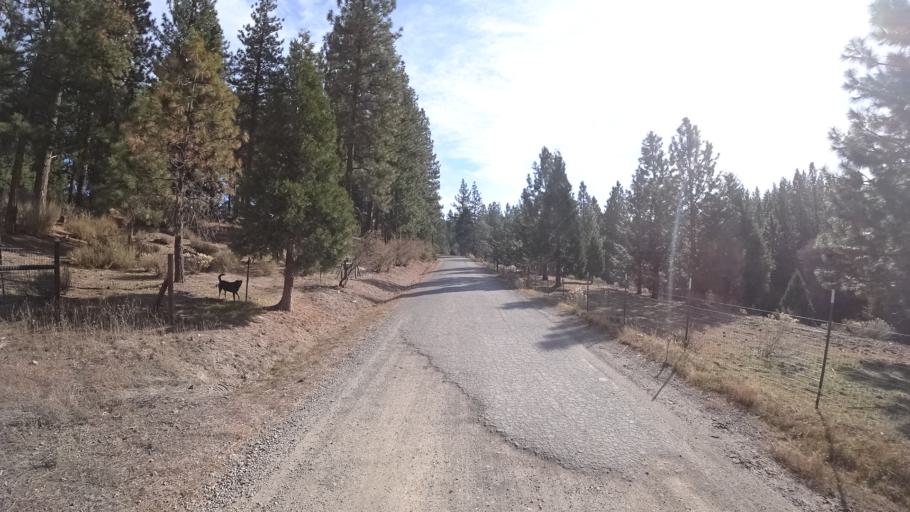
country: US
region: California
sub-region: Siskiyou County
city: Weed
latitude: 41.4336
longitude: -122.4222
